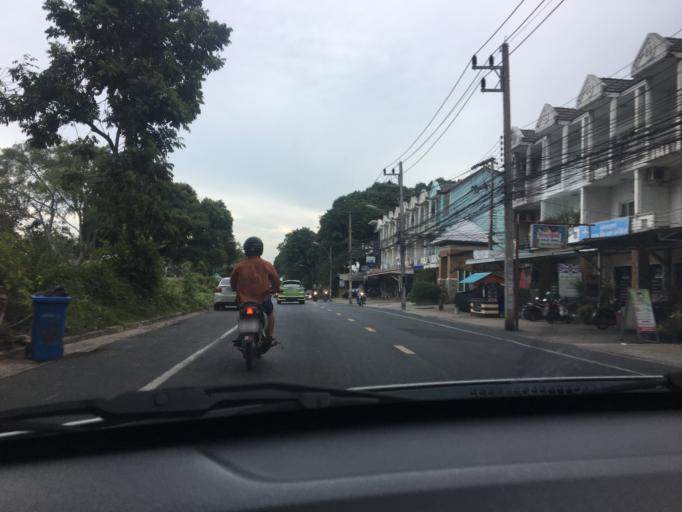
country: TH
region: Phuket
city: Phuket
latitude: 7.8947
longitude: 98.4021
